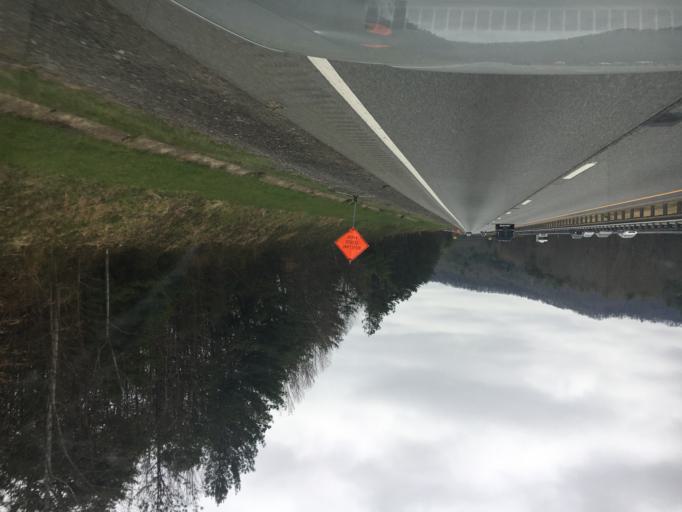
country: US
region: North Carolina
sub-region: Buncombe County
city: Weaverville
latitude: 35.7452
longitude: -82.5457
